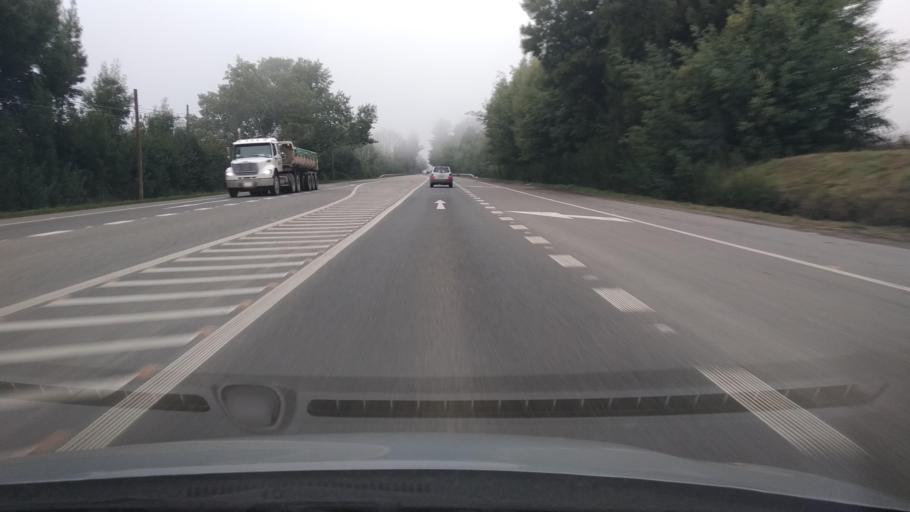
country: CL
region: Los Lagos
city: Las Animas
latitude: -39.7343
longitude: -73.2146
